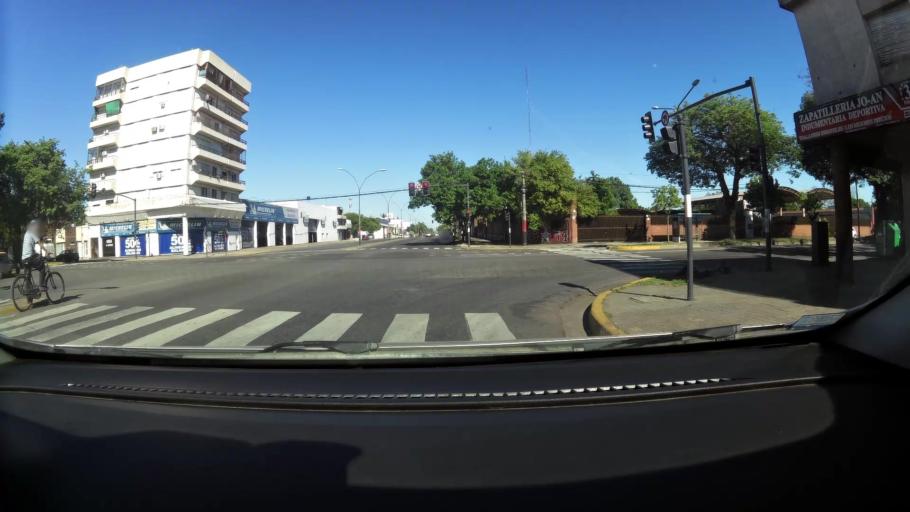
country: AR
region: Santa Fe
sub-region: Departamento de Rosario
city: Rosario
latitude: -32.9626
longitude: -60.6707
